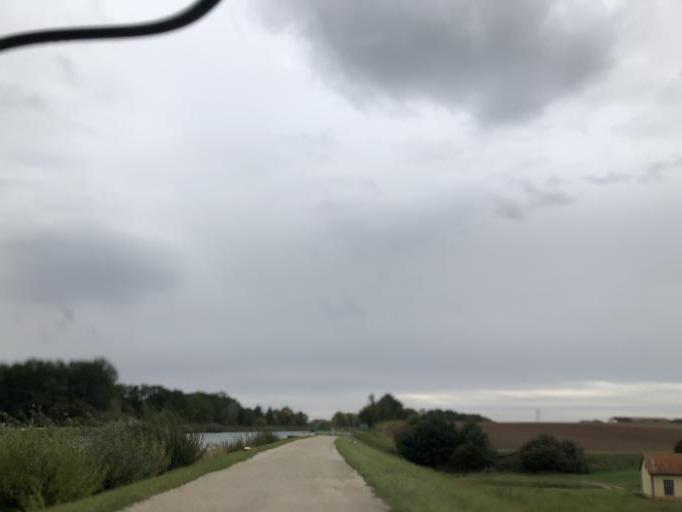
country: DE
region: Bavaria
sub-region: Regierungsbezirk Mittelfranken
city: Obermichelbach
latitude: 49.5407
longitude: 10.9686
